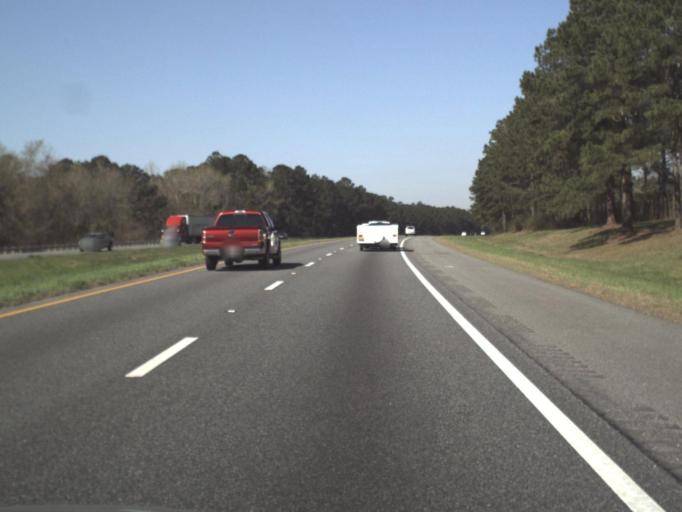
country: US
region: Florida
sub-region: Gadsden County
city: Quincy
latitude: 30.5308
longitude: -84.5681
